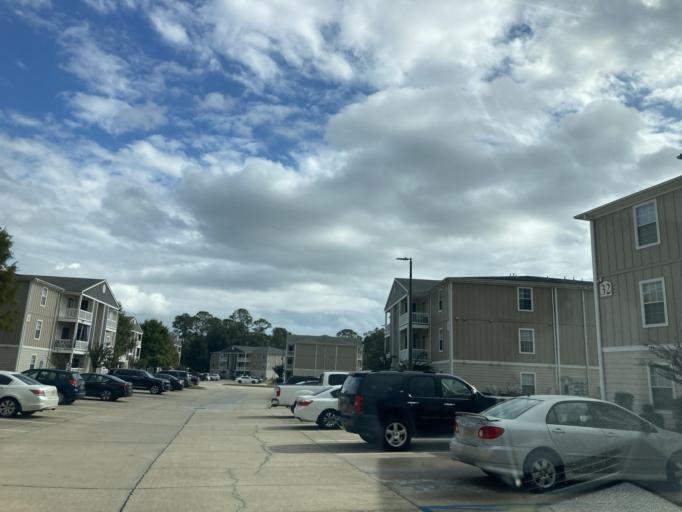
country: US
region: Mississippi
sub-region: Jackson County
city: Gulf Hills
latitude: 30.4377
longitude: -88.8348
